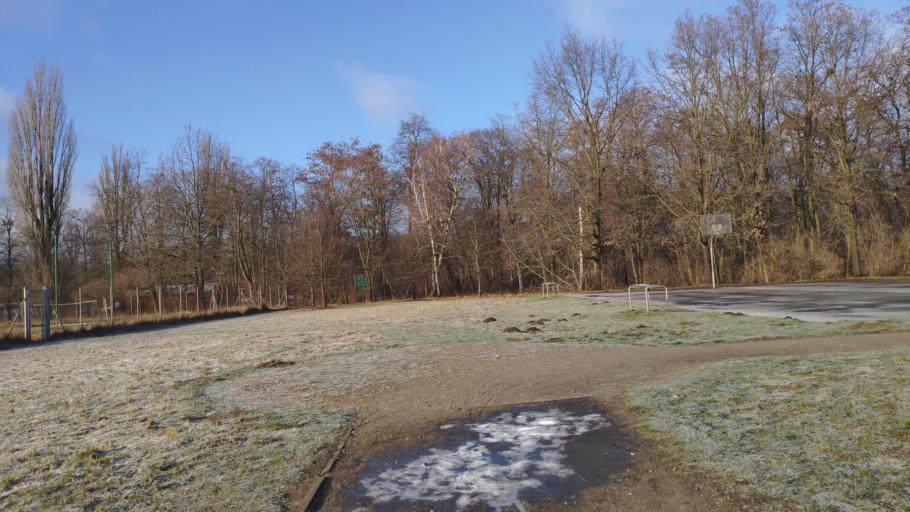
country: PL
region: Lodz Voivodeship
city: Lodz
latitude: 51.7724
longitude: 19.4127
